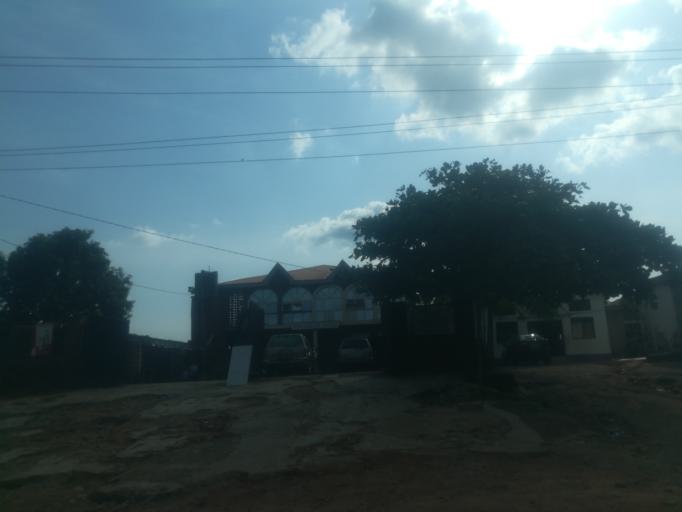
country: NG
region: Oyo
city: Ido
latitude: 7.3957
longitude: 3.8097
